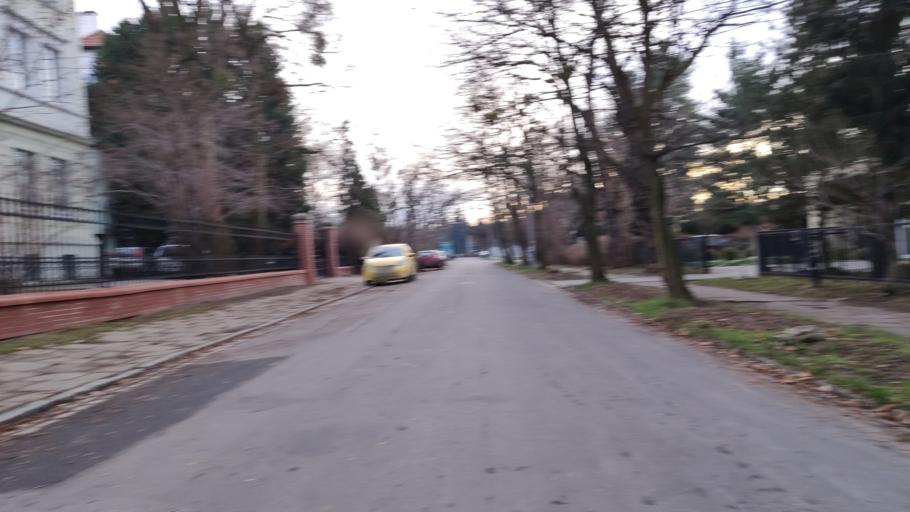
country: PL
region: Lower Silesian Voivodeship
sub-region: Powiat wroclawski
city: Wroclaw
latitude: 51.0828
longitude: 17.0151
